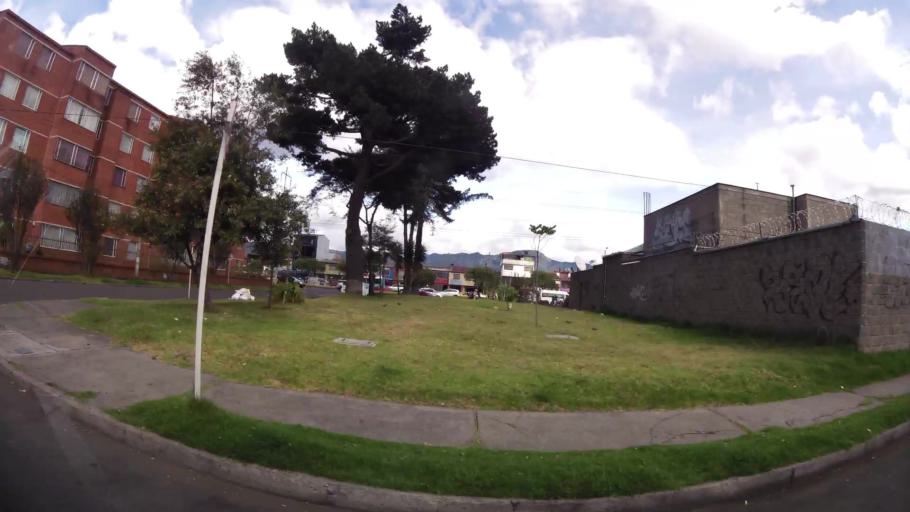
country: CO
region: Bogota D.C.
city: Bogota
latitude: 4.6125
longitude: -74.1287
